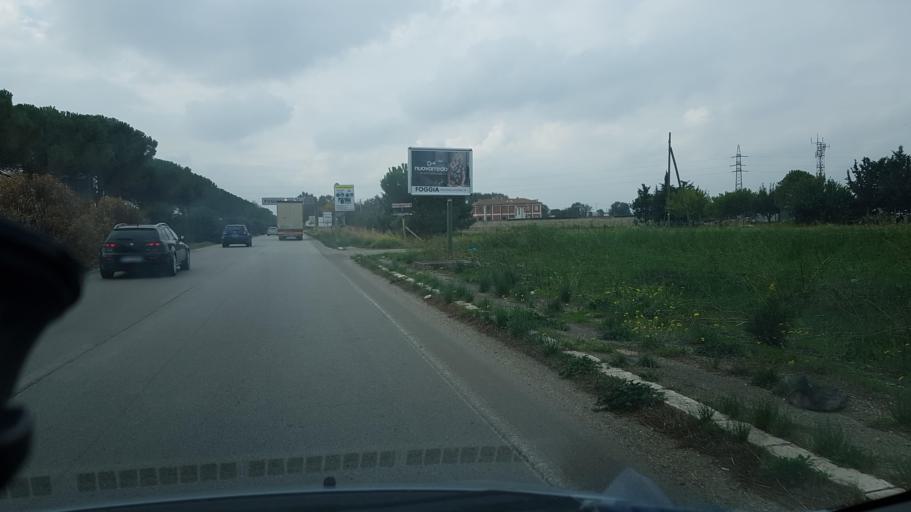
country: IT
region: Apulia
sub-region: Provincia di Foggia
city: Foggia
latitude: 41.4879
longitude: 15.5648
